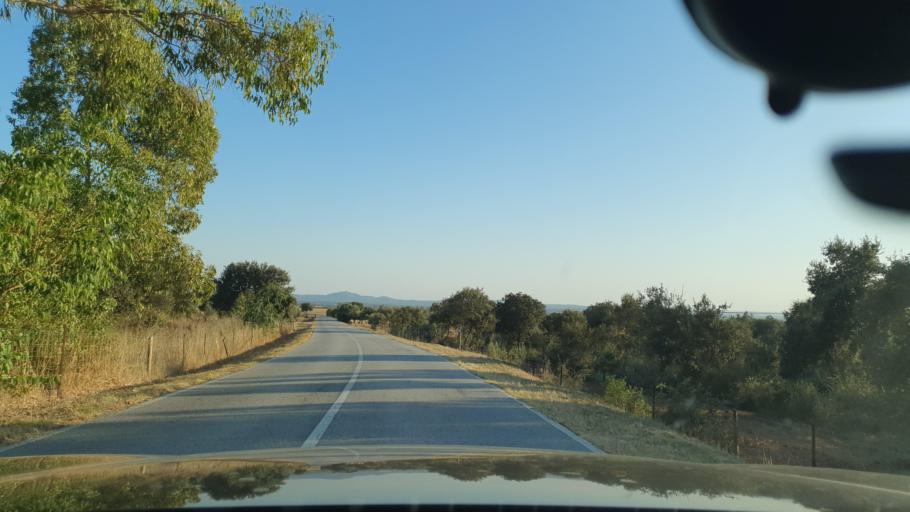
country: PT
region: Evora
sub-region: Estremoz
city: Estremoz
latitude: 38.9060
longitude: -7.6671
